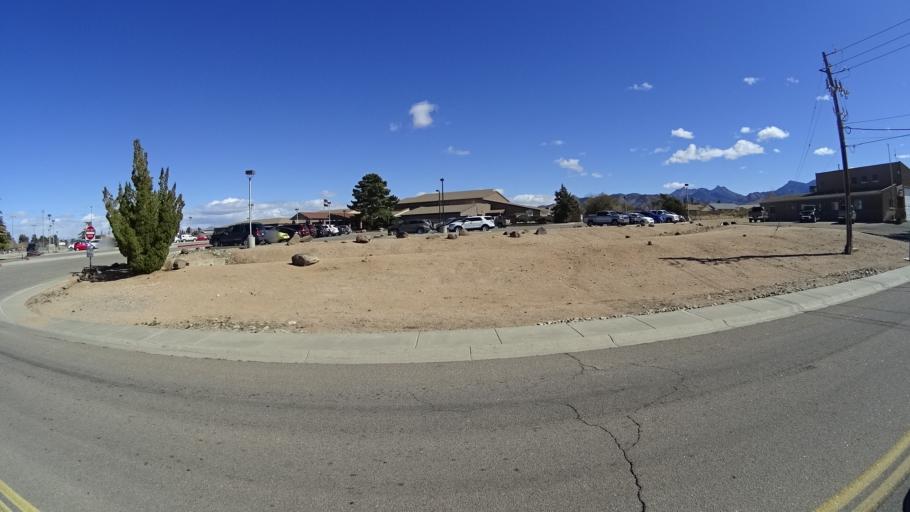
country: US
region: Arizona
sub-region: Mohave County
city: Kingman
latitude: 35.1928
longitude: -114.0113
